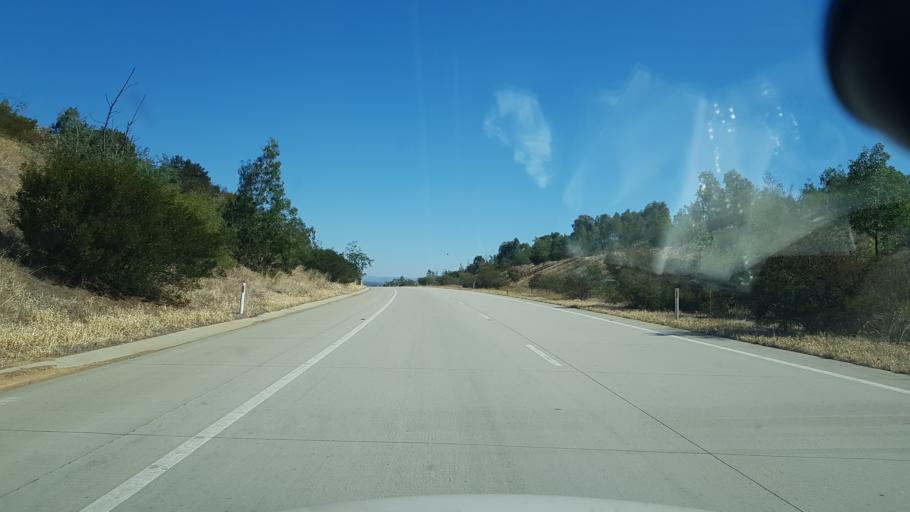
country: AU
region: New South Wales
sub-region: Albury Municipality
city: Lavington
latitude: -35.9182
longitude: 147.0980
